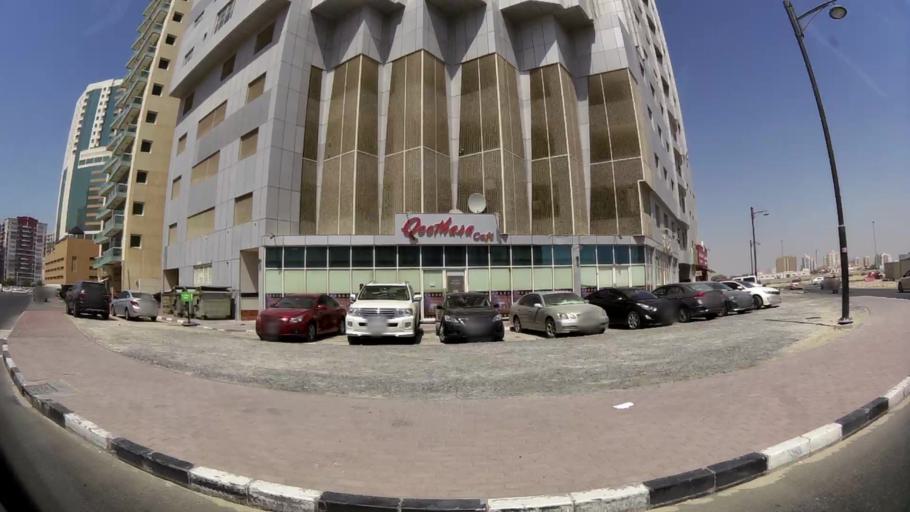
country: AE
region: Ash Shariqah
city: Sharjah
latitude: 25.2864
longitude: 55.3639
